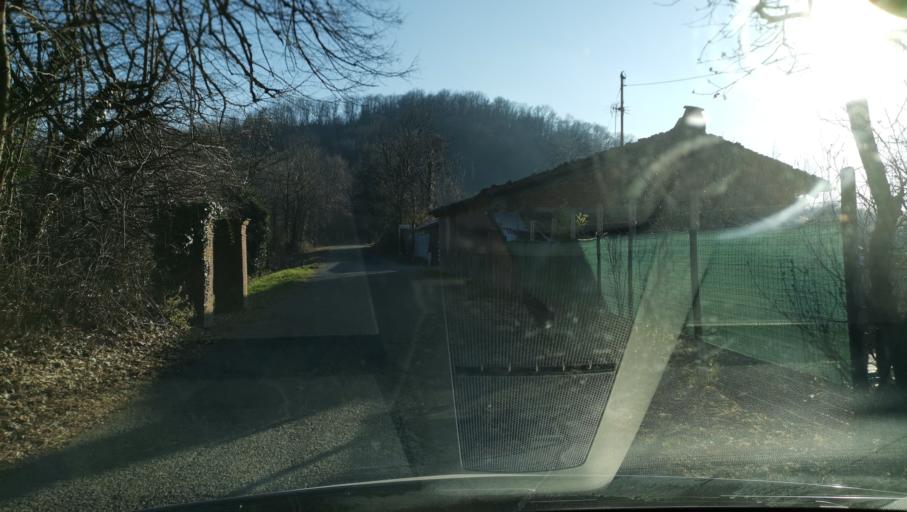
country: IT
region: Piedmont
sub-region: Provincia di Torino
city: Castagneto Po
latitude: 45.1428
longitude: 7.8872
